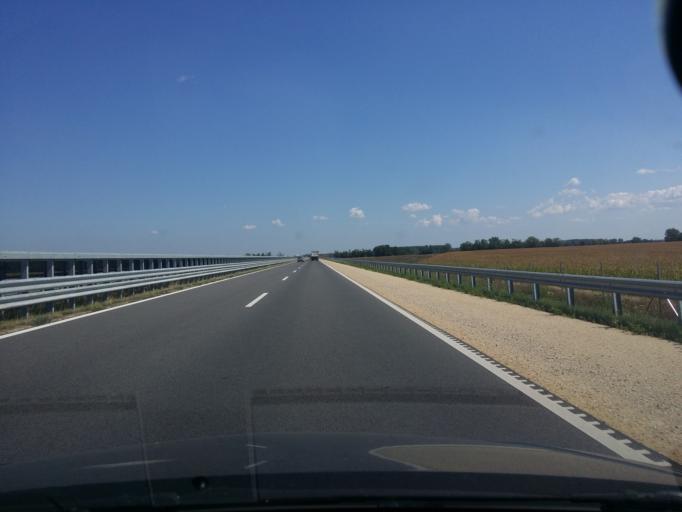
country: HU
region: Gyor-Moson-Sopron
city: Farad
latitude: 47.5218
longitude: 17.1963
